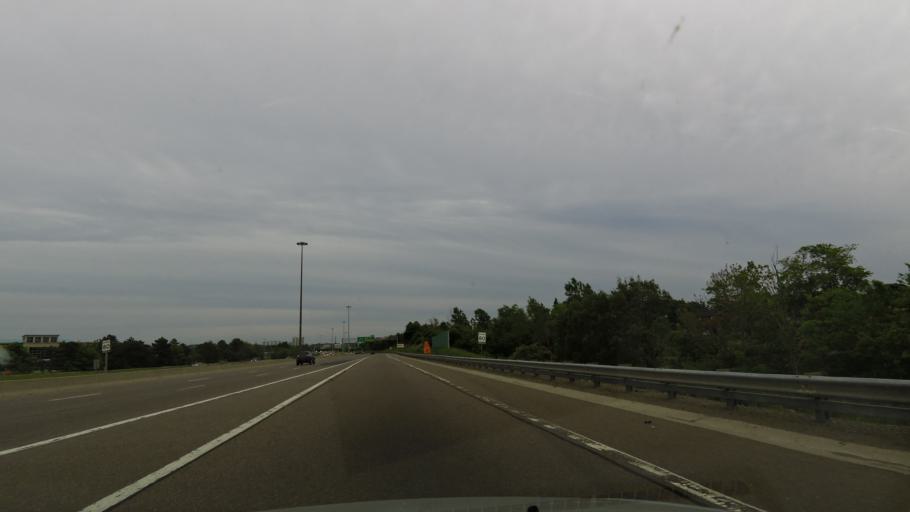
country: CA
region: Ontario
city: Etobicoke
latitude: 43.7138
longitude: -79.5163
